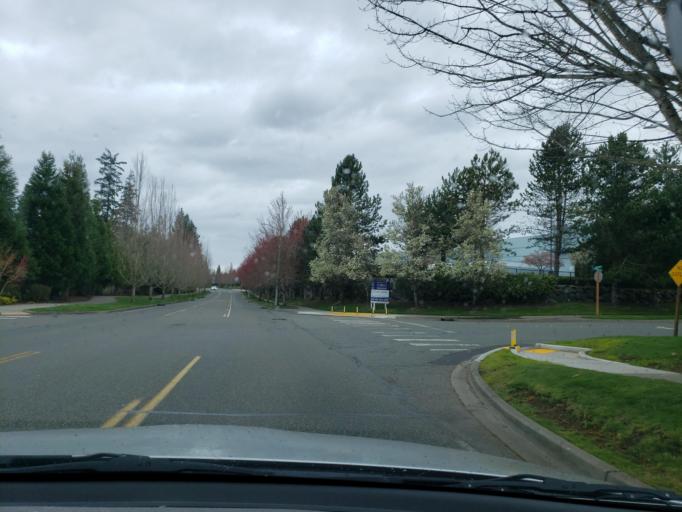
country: US
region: Washington
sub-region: Snohomish County
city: Meadowdale
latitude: 47.8897
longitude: -122.2952
